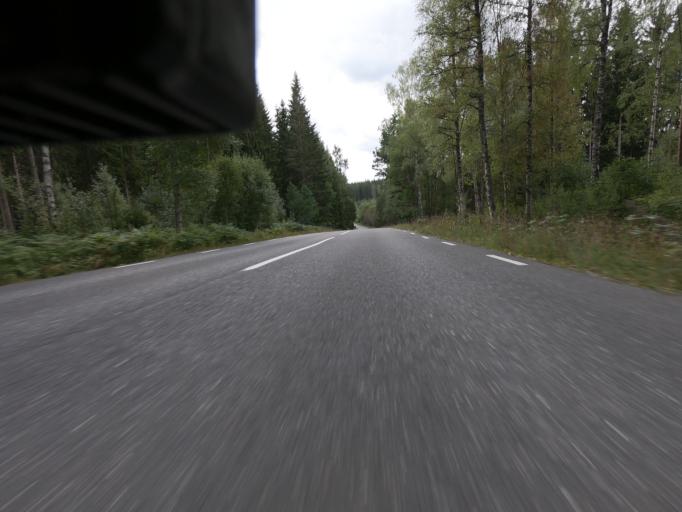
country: SE
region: Joenkoeping
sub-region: Vetlanda Kommun
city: Landsbro
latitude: 57.2474
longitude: 14.9468
